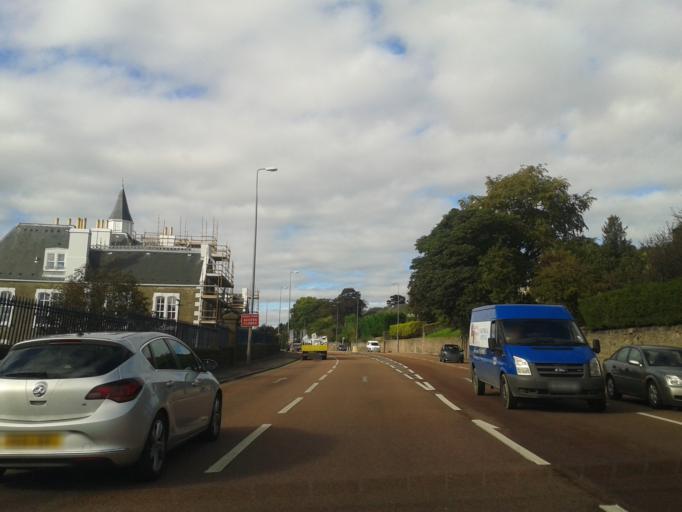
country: GB
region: Scotland
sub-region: Fife
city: Newport-On-Tay
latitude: 56.4685
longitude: -2.9356
